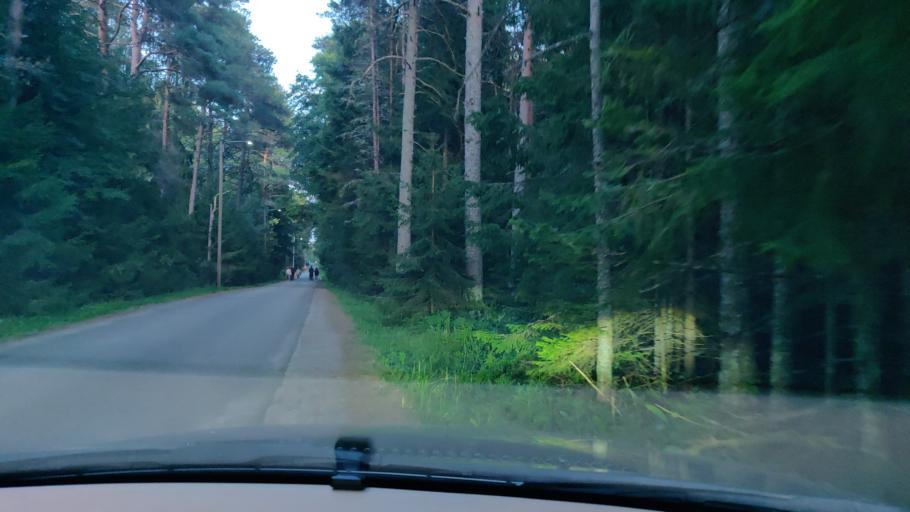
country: EE
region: Harju
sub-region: Keila linn
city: Keila
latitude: 59.3465
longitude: 24.2600
